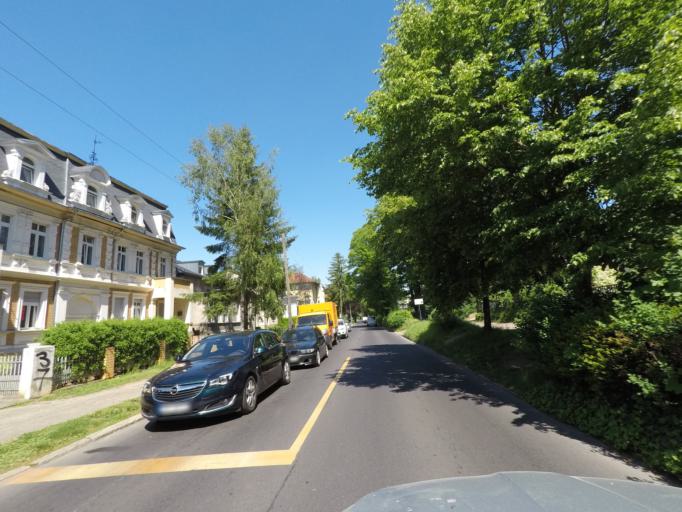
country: DE
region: Brandenburg
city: Eberswalde
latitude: 52.8279
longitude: 13.8096
